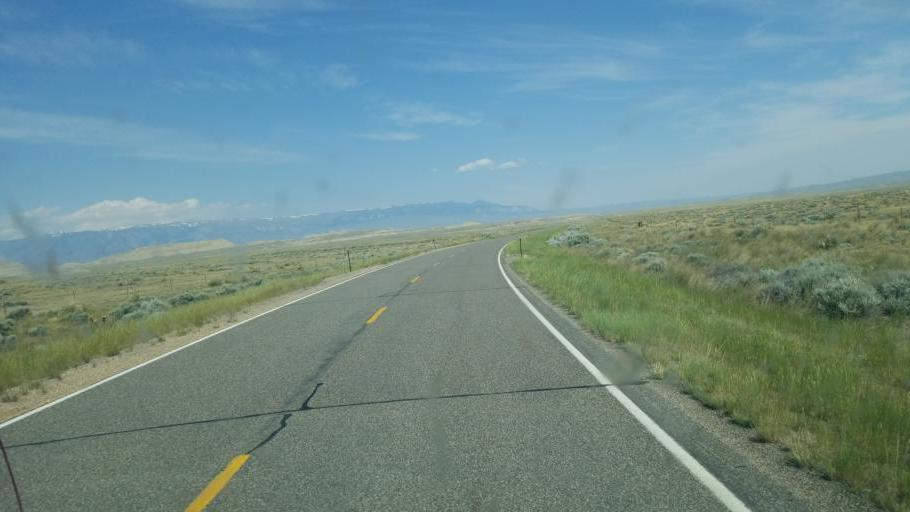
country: US
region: Wyoming
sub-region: Park County
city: Powell
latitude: 44.7975
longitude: -108.9585
